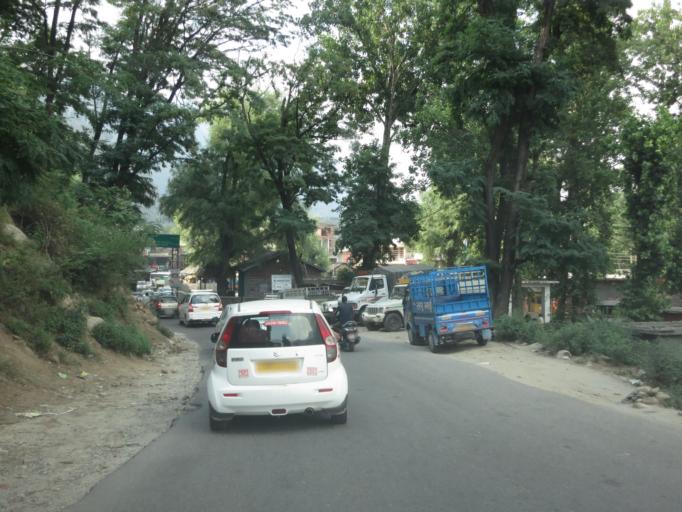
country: IN
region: Himachal Pradesh
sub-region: Kulu
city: Nagar
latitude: 32.1136
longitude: 77.1469
